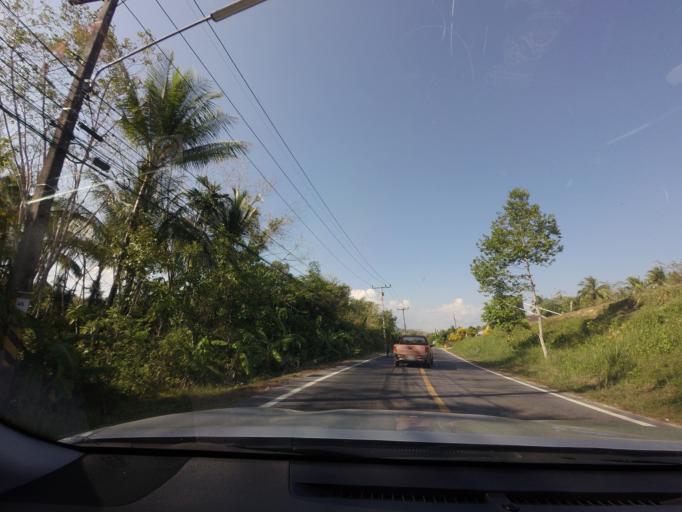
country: TH
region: Phangnga
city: Takua Thung
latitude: 8.2688
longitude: 98.3715
